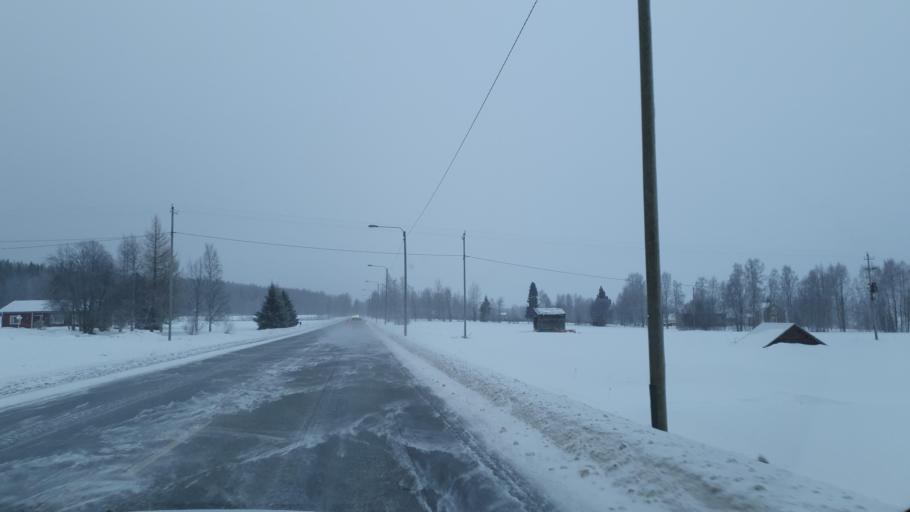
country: FI
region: Lapland
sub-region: Torniolaakso
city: Ylitornio
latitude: 66.1227
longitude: 23.9471
